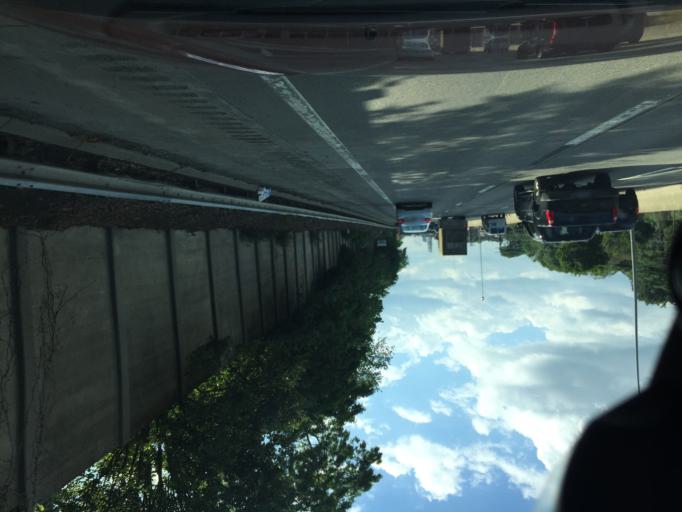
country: US
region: New York
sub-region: Westchester County
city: Larchmont
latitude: 40.9387
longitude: -73.7544
